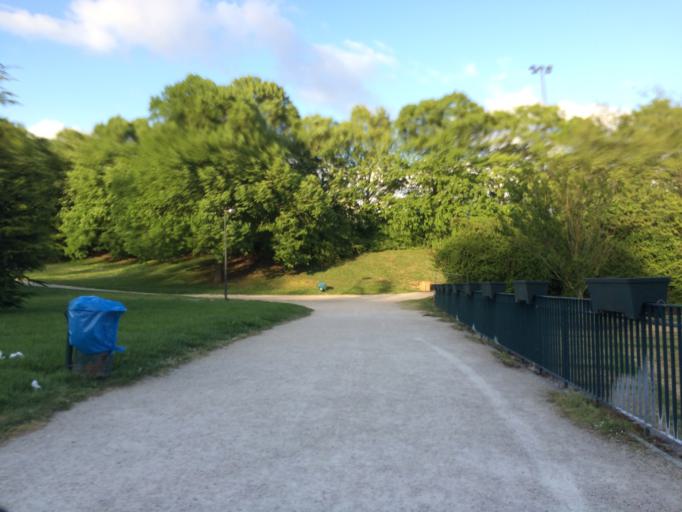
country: FR
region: Ile-de-France
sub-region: Departement de l'Essonne
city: Massy
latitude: 48.7298
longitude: 2.2913
